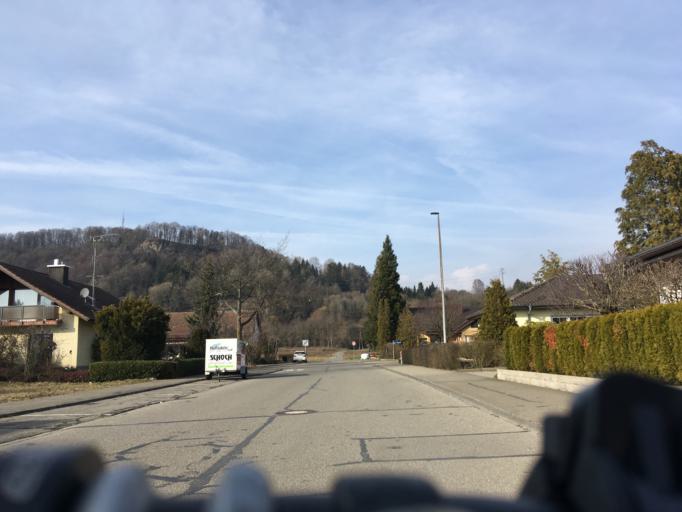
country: DE
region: Baden-Wuerttemberg
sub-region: Freiburg Region
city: Rielasingen-Worblingen
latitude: 47.7299
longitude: 8.8310
